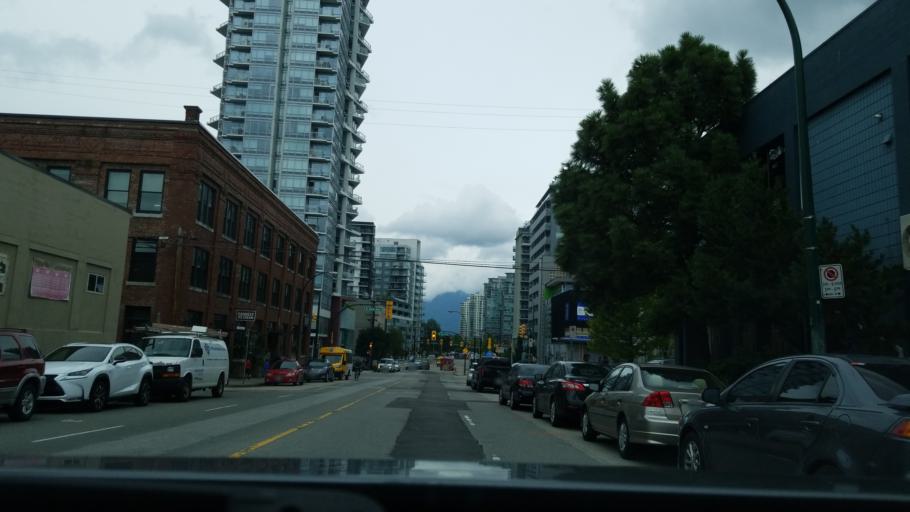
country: CA
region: British Columbia
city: Vancouver
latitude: 49.2684
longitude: -123.1027
